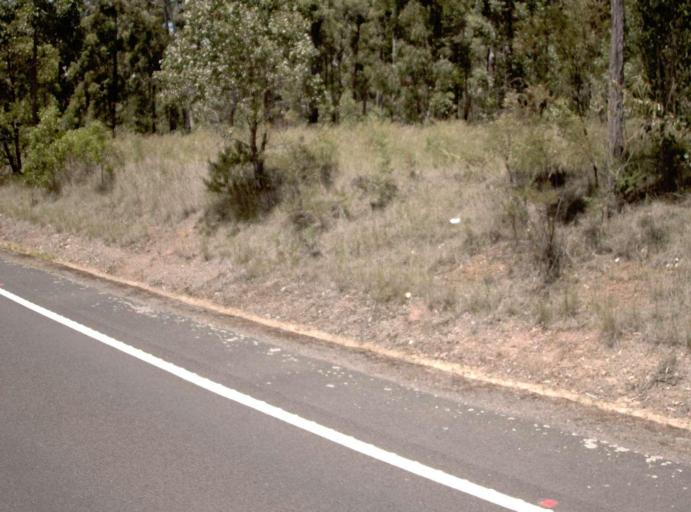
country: AU
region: Victoria
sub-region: East Gippsland
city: Lakes Entrance
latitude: -37.7454
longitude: 148.3848
